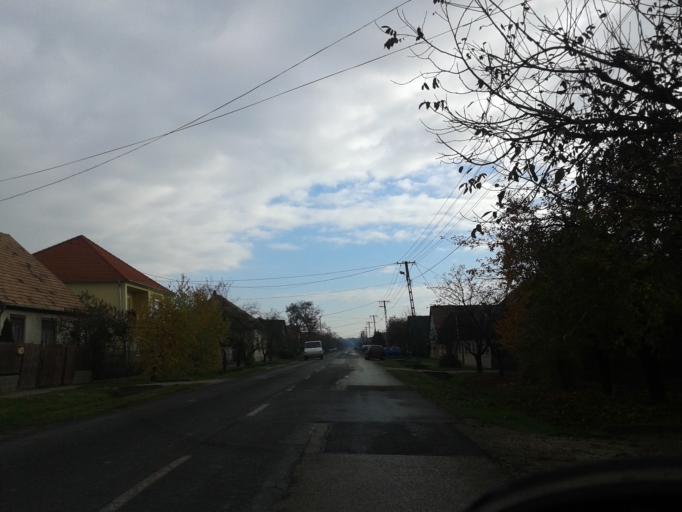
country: HU
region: Fejer
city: Adony
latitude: 47.1234
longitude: 18.8466
